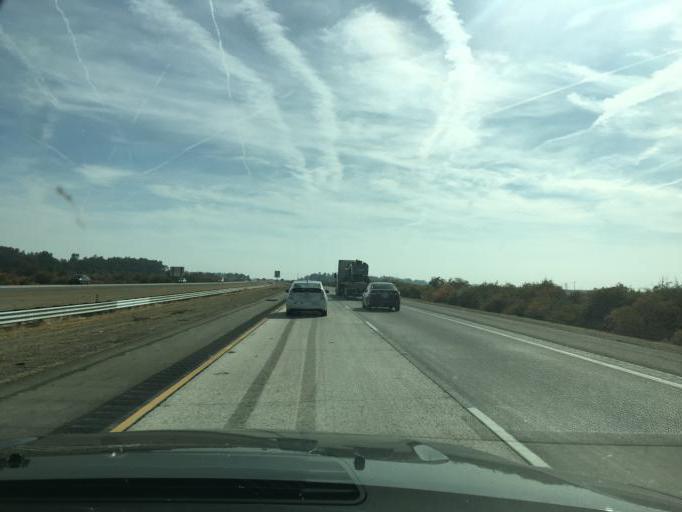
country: US
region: California
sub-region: Kern County
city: Lost Hills
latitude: 35.6076
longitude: -119.6470
